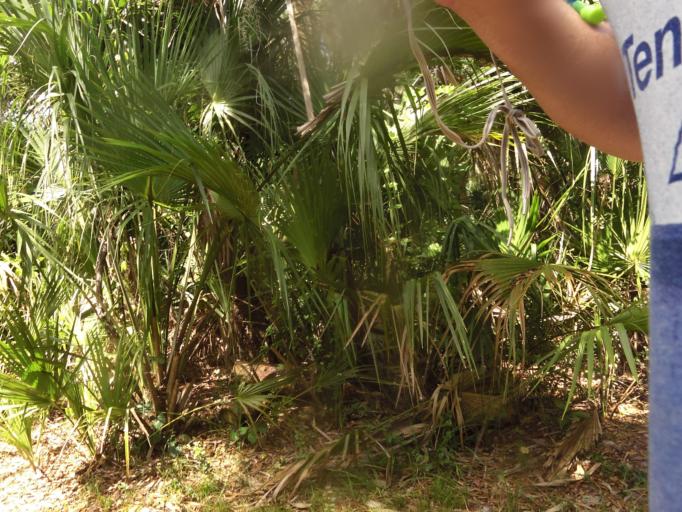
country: US
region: Florida
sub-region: Flagler County
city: Palm Coast
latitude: 29.6285
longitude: -81.2086
